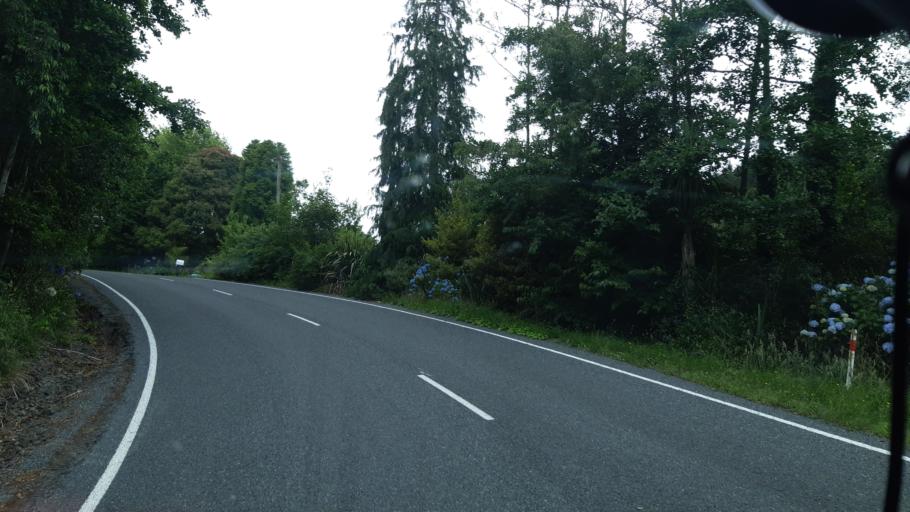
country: NZ
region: Waikato
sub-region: Waikato District
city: Raglan
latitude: -37.8480
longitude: 175.0428
